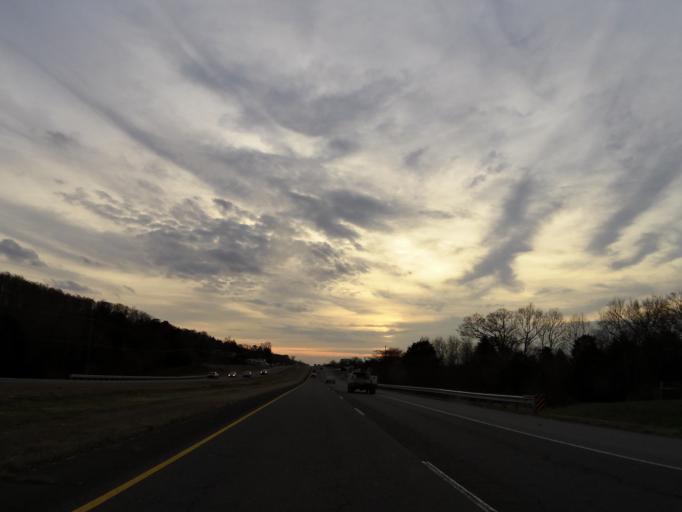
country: US
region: Tennessee
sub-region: Monroe County
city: Vonore
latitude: 35.5668
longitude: -84.2906
